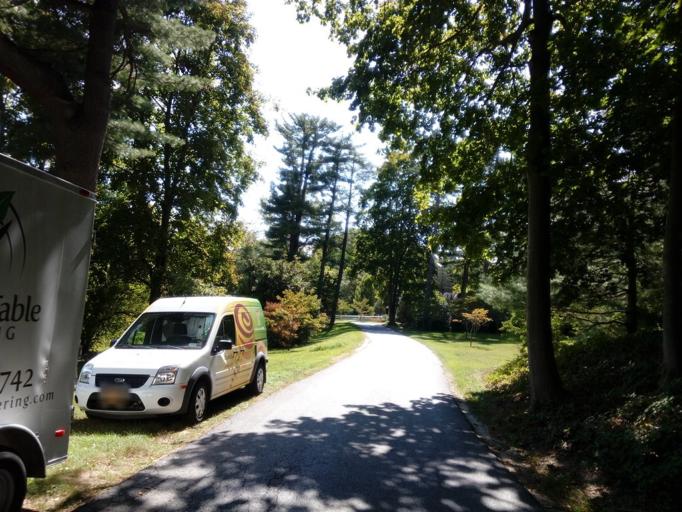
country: US
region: New York
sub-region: Nassau County
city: Laurel Hollow
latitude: 40.8658
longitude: -73.4724
